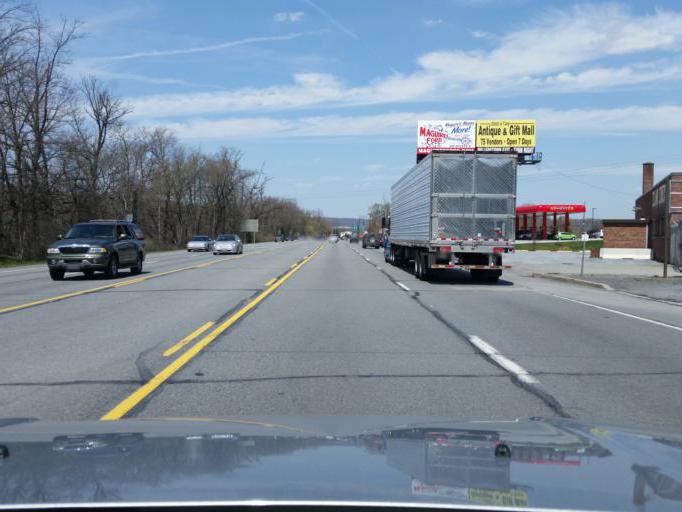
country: US
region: Pennsylvania
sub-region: Perry County
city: Duncannon
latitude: 40.4077
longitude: -77.0104
